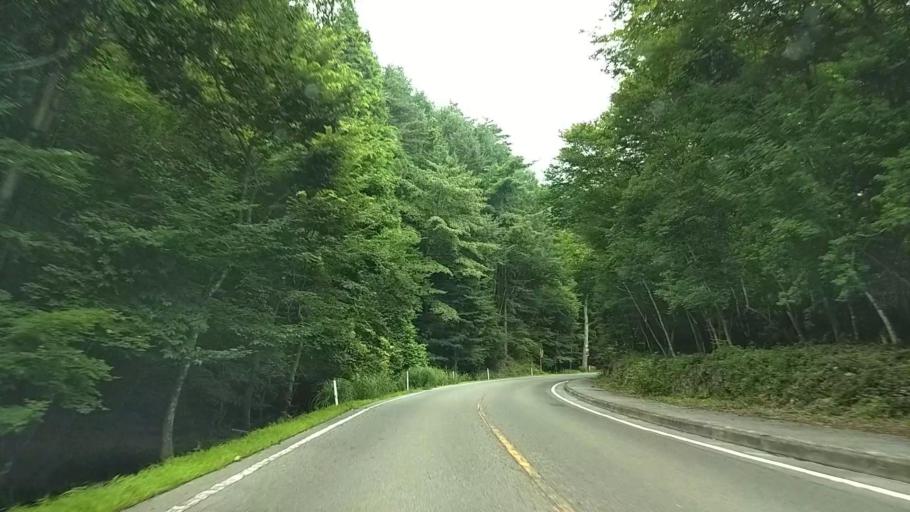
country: JP
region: Yamanashi
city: Fujikawaguchiko
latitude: 35.4960
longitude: 138.6494
